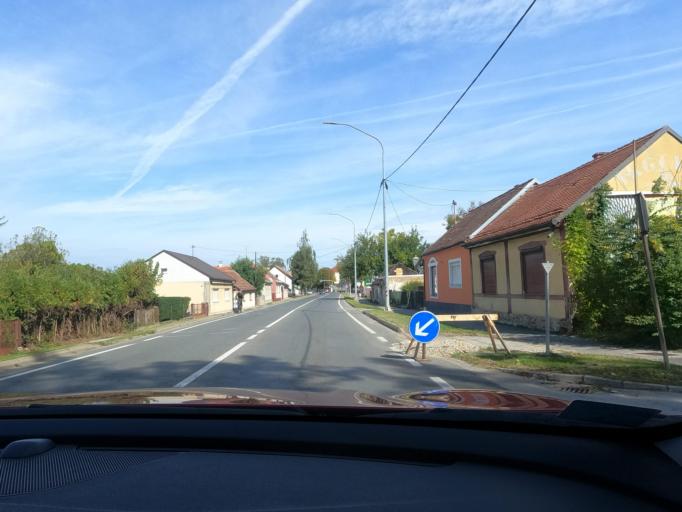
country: HR
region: Sisacko-Moslavacka
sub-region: Grad Sisak
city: Sisak
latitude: 45.4744
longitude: 16.3673
